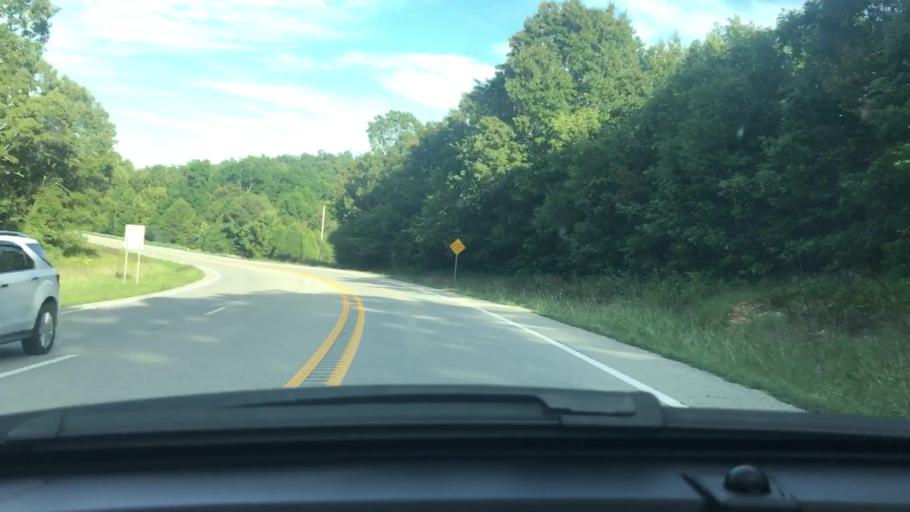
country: US
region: Arkansas
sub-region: Sharp County
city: Cherokee Village
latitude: 36.2733
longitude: -91.3554
